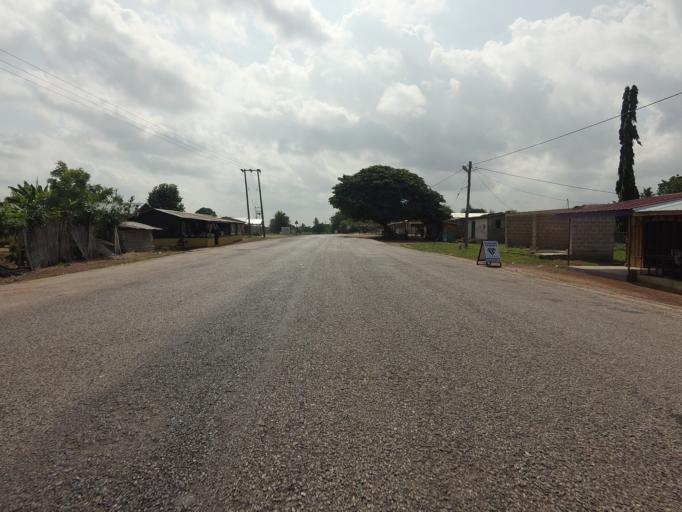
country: GH
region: Volta
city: Ho
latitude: 6.4148
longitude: 0.7560
